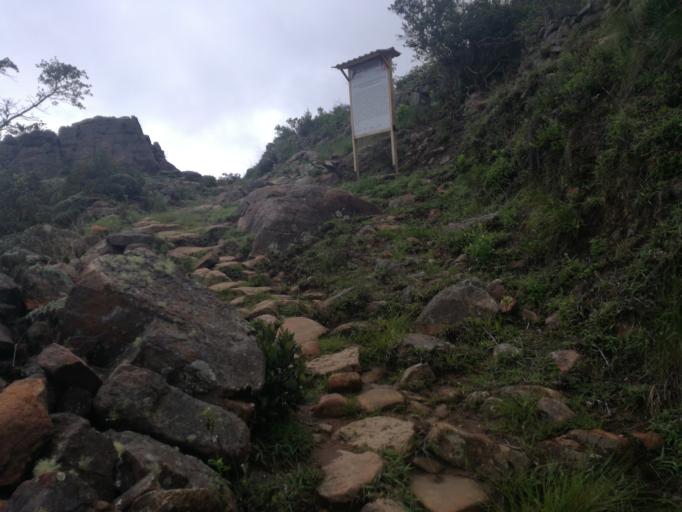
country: CO
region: Boyaca
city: Socha Viejo
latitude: 6.0024
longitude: -72.6851
